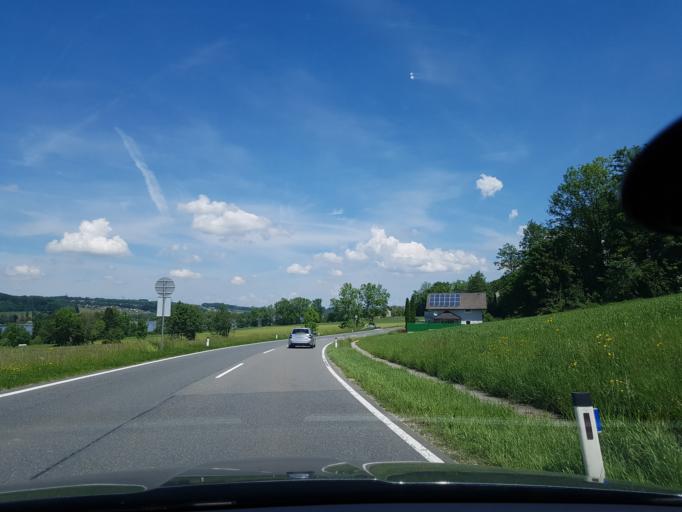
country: AT
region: Salzburg
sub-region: Politischer Bezirk Salzburg-Umgebung
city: Obertrum am See
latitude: 47.9450
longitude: 13.0881
